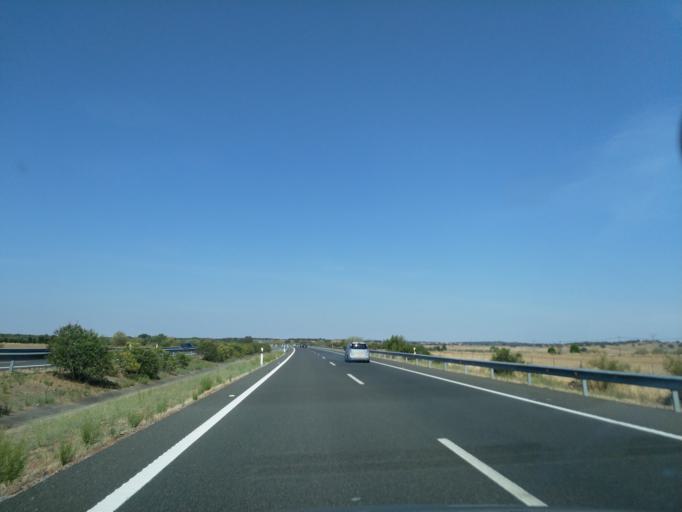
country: ES
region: Extremadura
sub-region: Provincia de Caceres
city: Casas de Don Antonio
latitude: 39.2543
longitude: -6.3100
